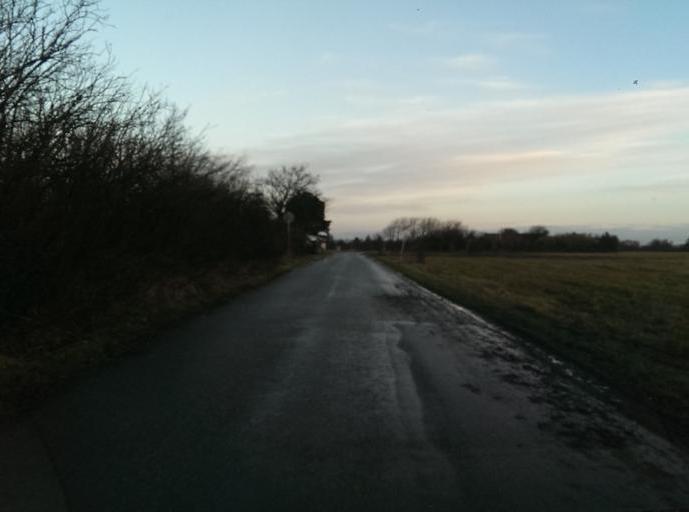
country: DK
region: South Denmark
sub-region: Esbjerg Kommune
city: Tjaereborg
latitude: 55.4657
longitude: 8.6298
